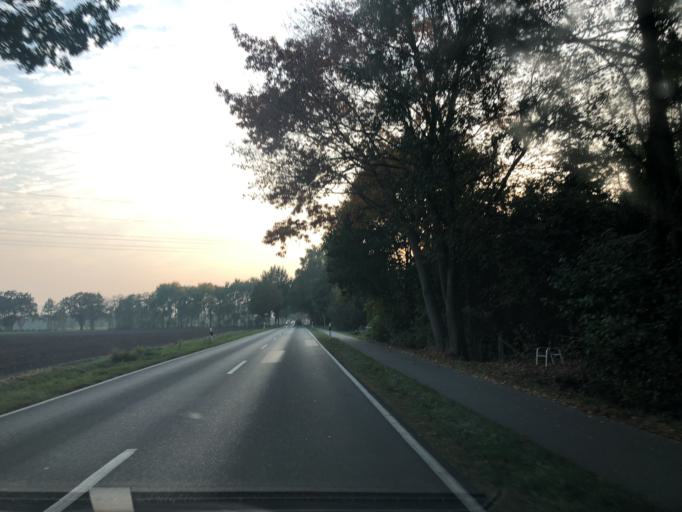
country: DE
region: Lower Saxony
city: Wardenburg
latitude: 53.0881
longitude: 8.1796
